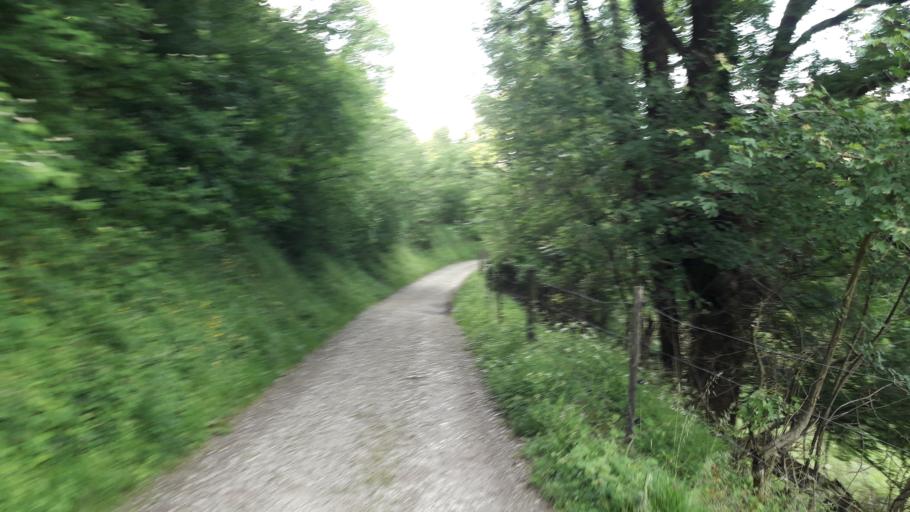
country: FR
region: Rhone-Alpes
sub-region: Departement de l'Isere
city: Gieres
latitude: 45.1702
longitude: 5.7852
